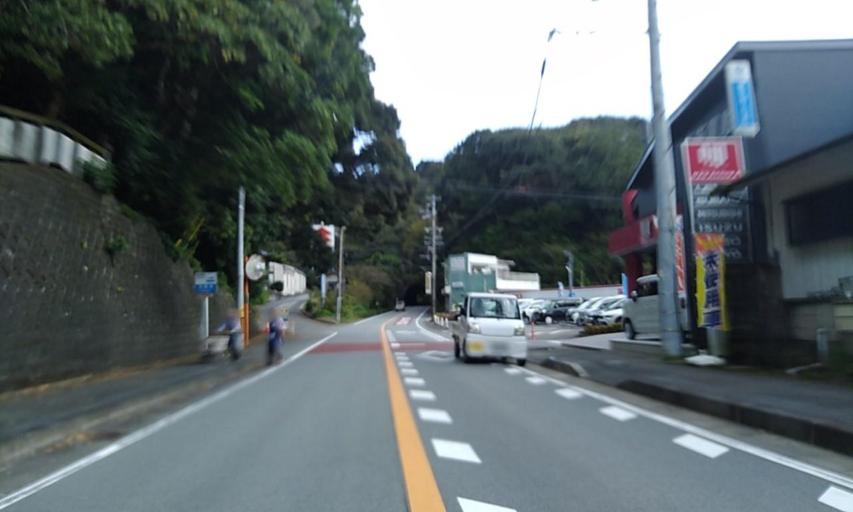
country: JP
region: Mie
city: Ise
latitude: 34.2836
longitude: 136.5424
